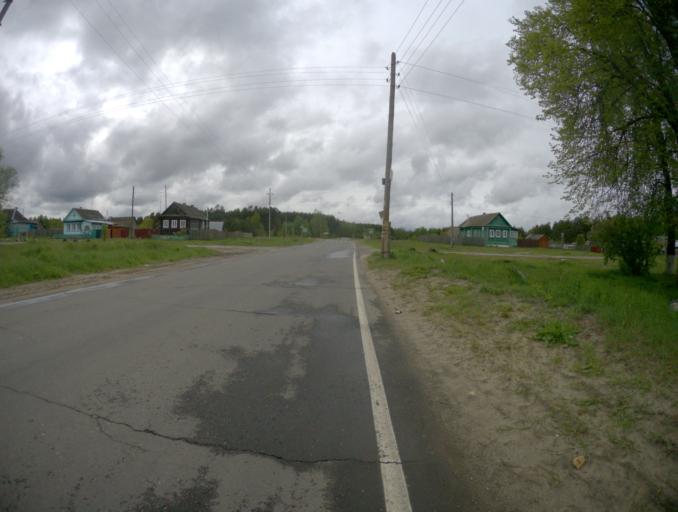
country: RU
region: Vladimir
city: Velikodvorskiy
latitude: 55.3879
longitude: 40.7414
